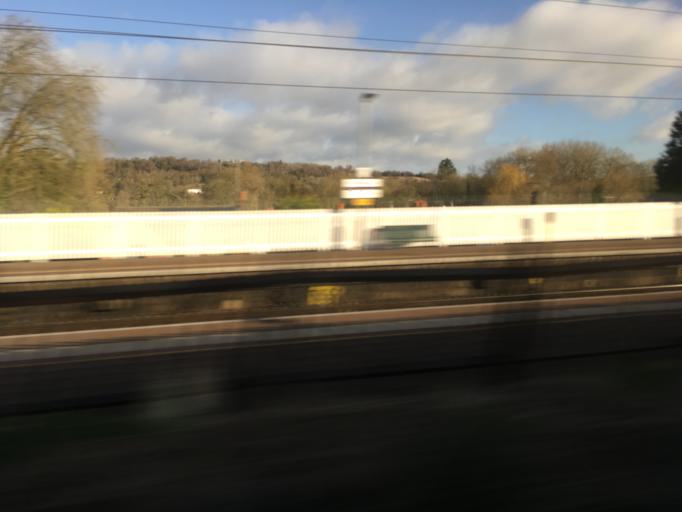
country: GB
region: England
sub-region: West Berkshire
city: Pangbourne
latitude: 51.4854
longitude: -1.0907
